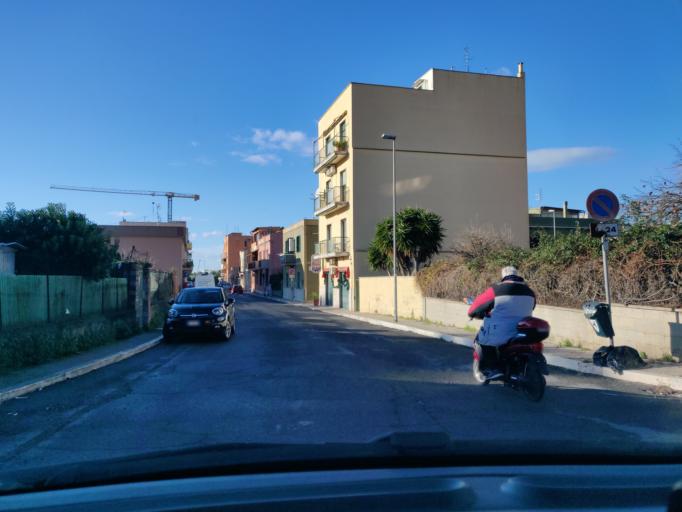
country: IT
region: Latium
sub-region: Citta metropolitana di Roma Capitale
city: Civitavecchia
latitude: 42.0991
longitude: 11.7938
